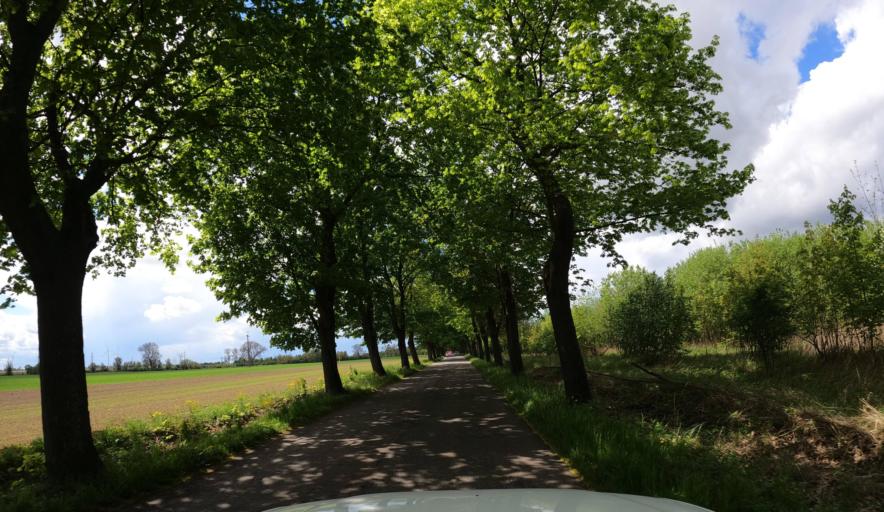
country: PL
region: West Pomeranian Voivodeship
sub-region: Powiat kamienski
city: Wolin
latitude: 53.8587
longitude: 14.6387
